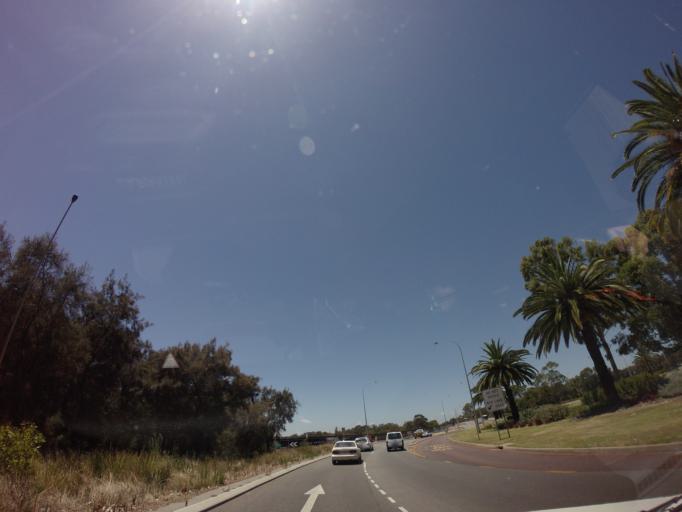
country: AU
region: Western Australia
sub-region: City of Perth
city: East Perth
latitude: -31.9621
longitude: 115.8791
